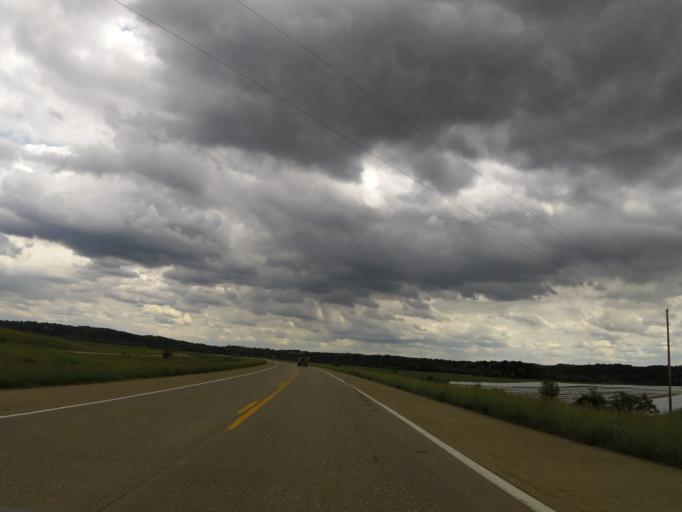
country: US
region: West Virginia
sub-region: Jackson County
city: Ravenswood
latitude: 38.9361
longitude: -81.7864
